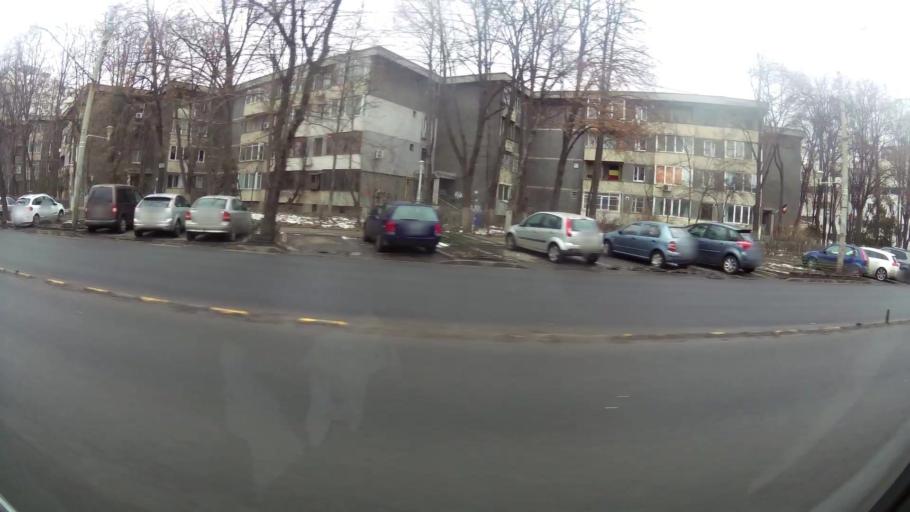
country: RO
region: Ilfov
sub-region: Comuna Chiajna
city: Rosu
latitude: 44.4180
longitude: 26.0382
